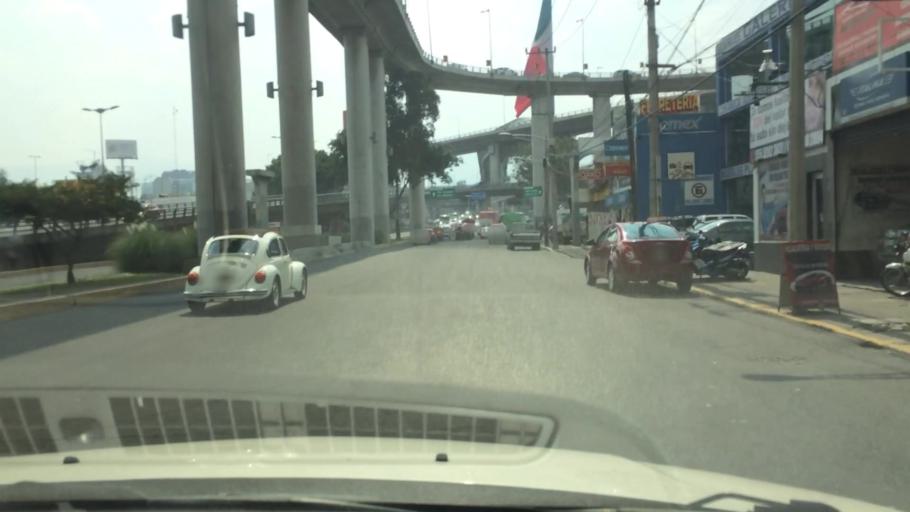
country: MX
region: Mexico City
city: Magdalena Contreras
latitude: 19.3320
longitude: -99.2084
